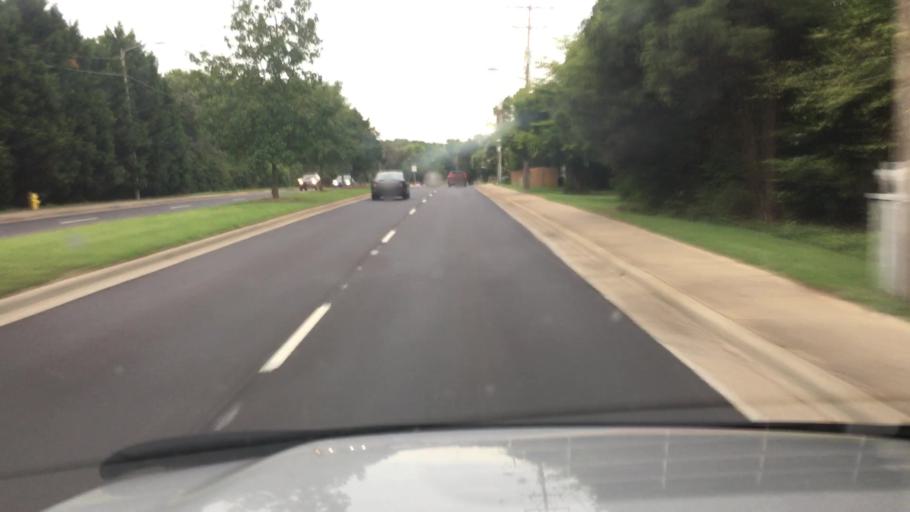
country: US
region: North Carolina
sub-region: Mecklenburg County
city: Pineville
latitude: 35.0965
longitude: -80.8403
